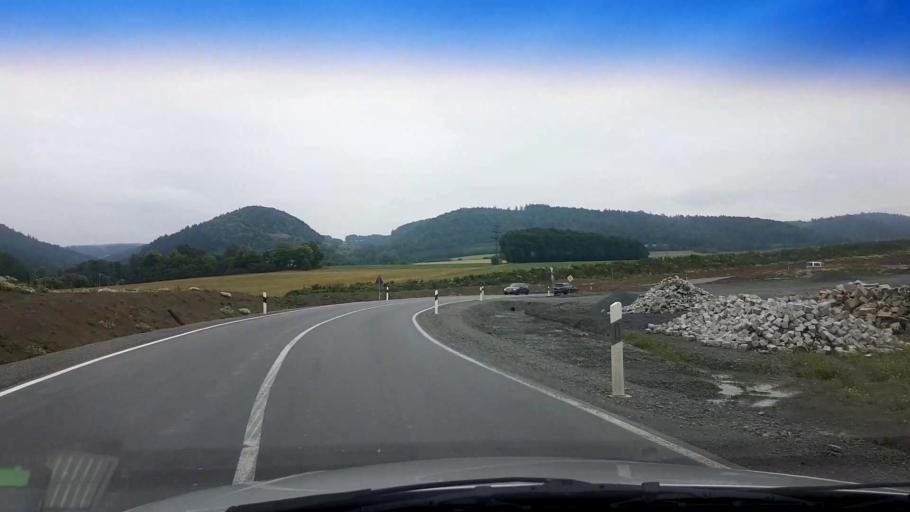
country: DE
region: Bavaria
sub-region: Upper Franconia
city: Untersteinach
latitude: 50.1326
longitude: 11.5361
